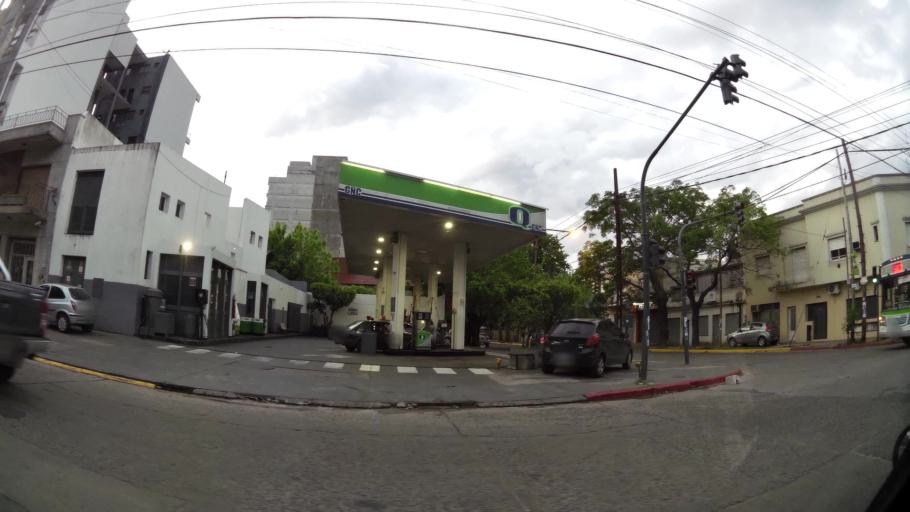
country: AR
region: Buenos Aires
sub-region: Partido de Quilmes
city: Quilmes
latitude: -34.7311
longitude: -58.2466
